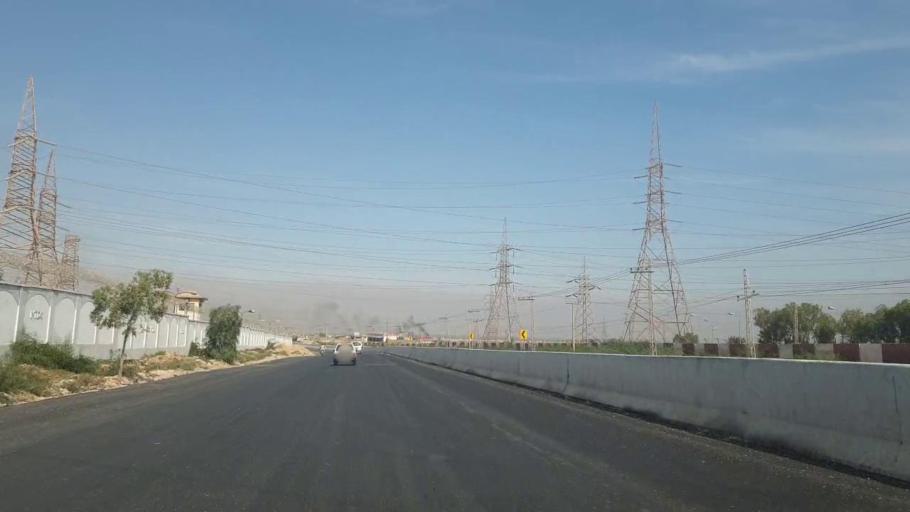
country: PK
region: Sindh
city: Jamshoro
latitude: 25.4760
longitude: 68.2714
